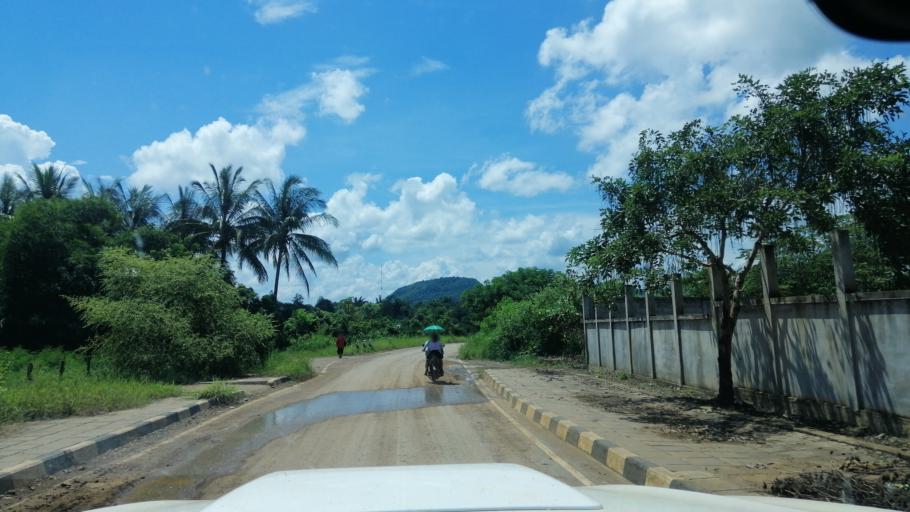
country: TH
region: Uttaradit
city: Ban Khok
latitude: 18.1351
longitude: 101.2768
